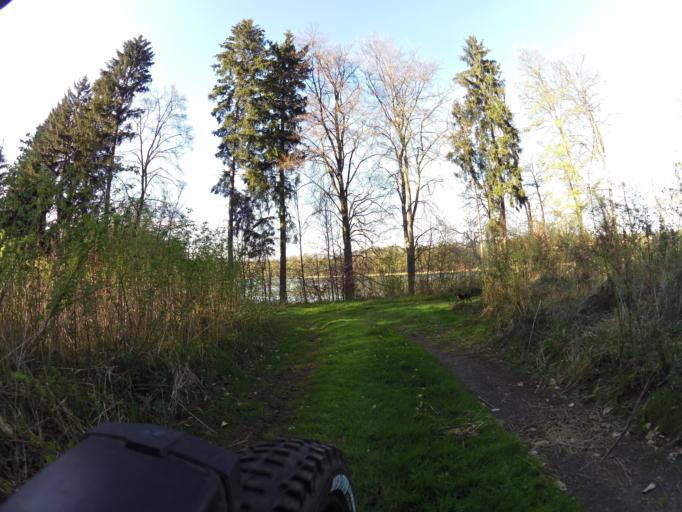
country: PL
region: West Pomeranian Voivodeship
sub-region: Powiat lobeski
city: Lobez
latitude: 53.7438
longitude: 15.6275
